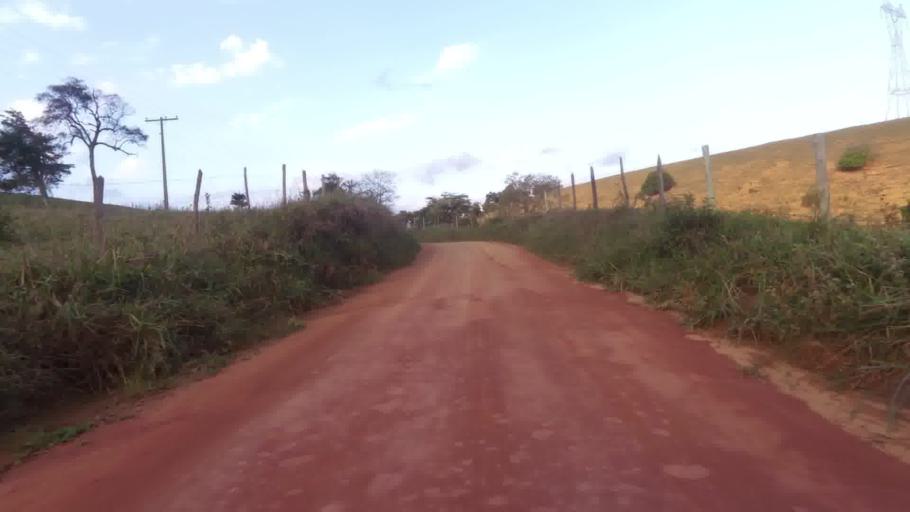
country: BR
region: Espirito Santo
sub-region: Guarapari
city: Guarapari
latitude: -20.6790
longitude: -40.6237
